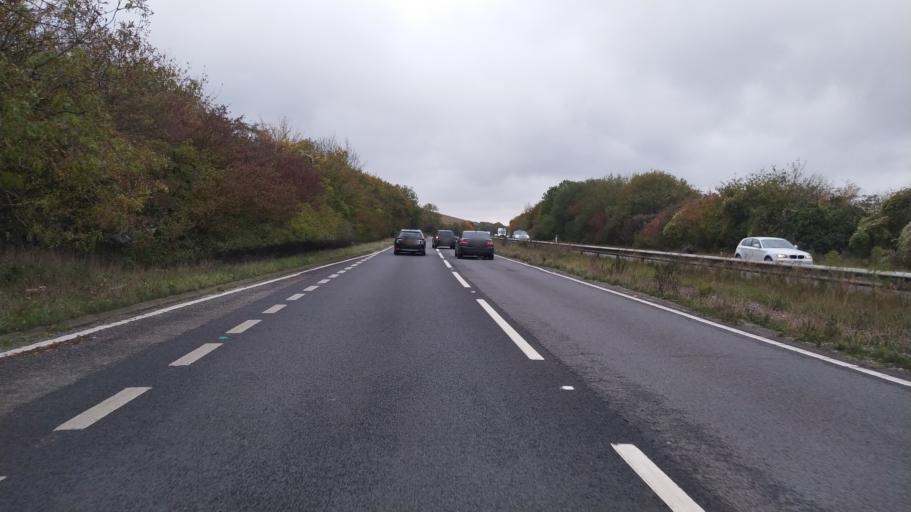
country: GB
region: England
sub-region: Hampshire
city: Cowplain
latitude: 50.9458
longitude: -0.9832
